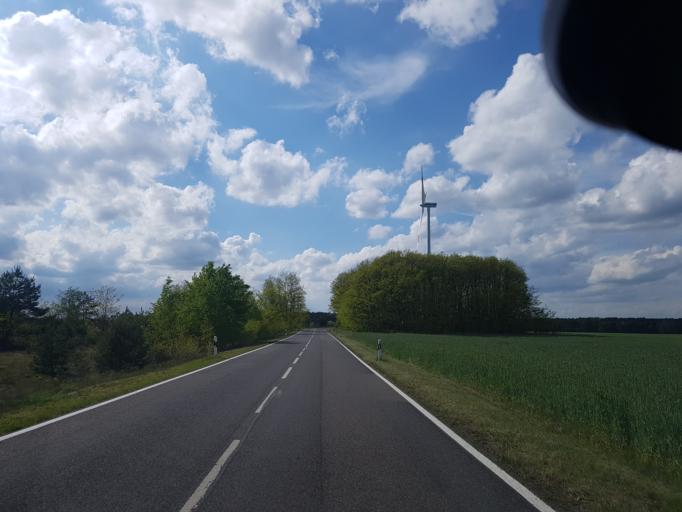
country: DE
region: Brandenburg
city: Drebkau
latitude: 51.6535
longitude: 14.2842
